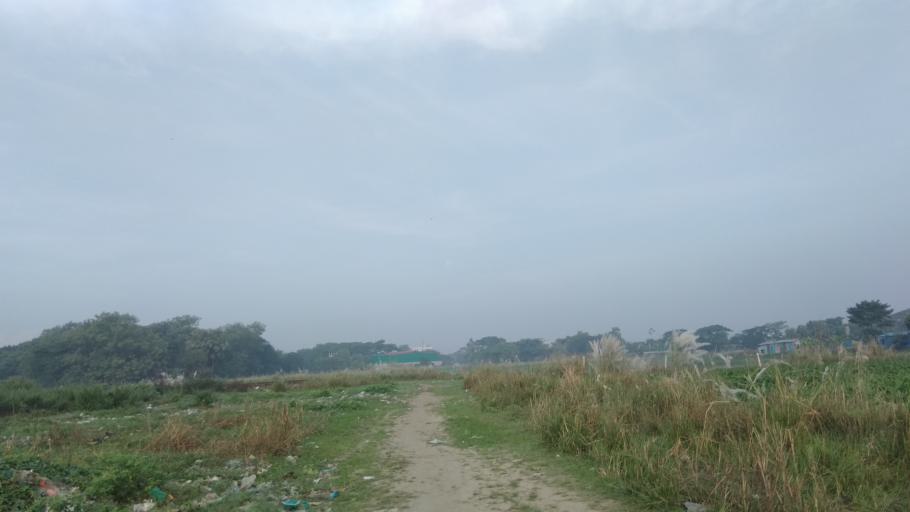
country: BD
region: Dhaka
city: Tungi
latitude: 23.8508
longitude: 90.4439
